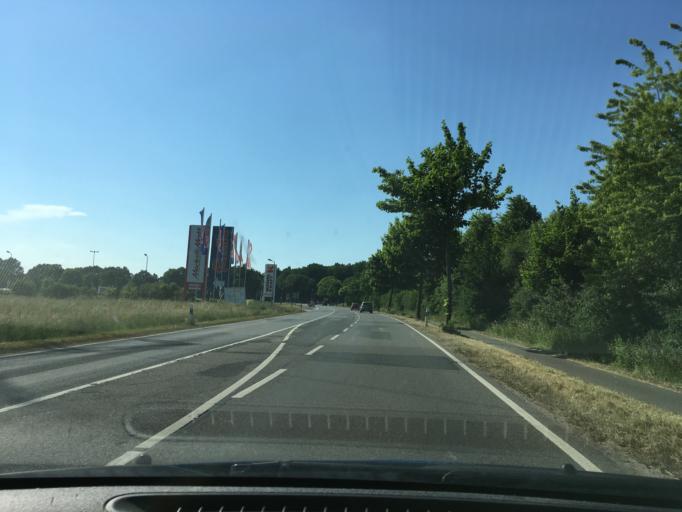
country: DE
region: Lower Saxony
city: Buchholz in der Nordheide
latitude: 53.3519
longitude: 9.8656
